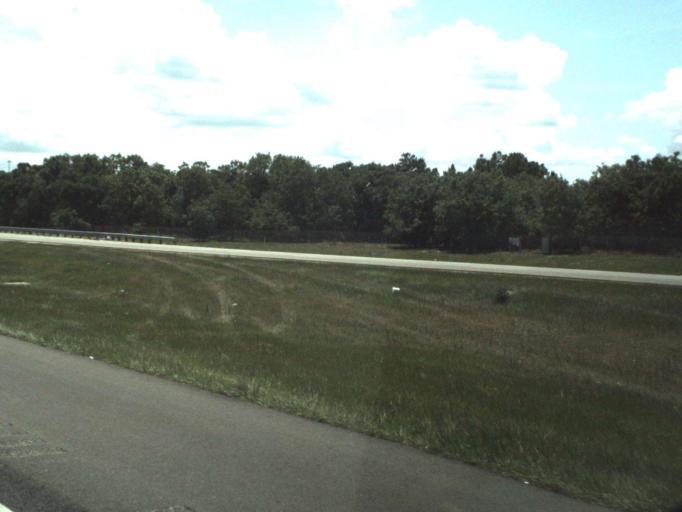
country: US
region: Florida
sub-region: Seminole County
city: Heathrow
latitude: 28.7999
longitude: -81.3439
